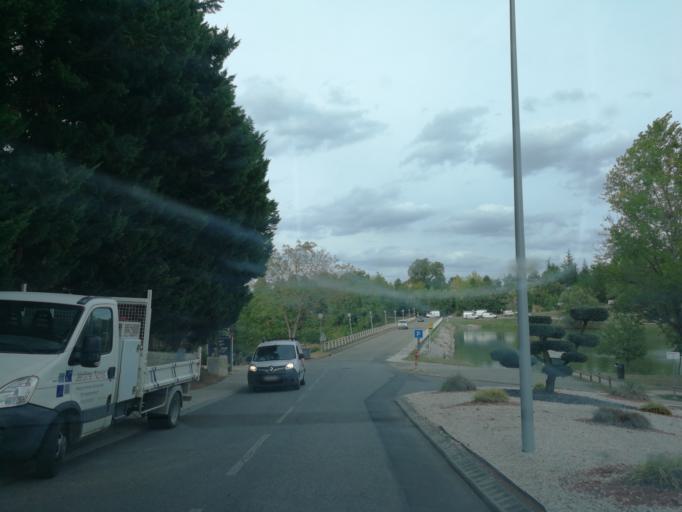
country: FR
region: Midi-Pyrenees
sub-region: Departement de la Haute-Garonne
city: Flourens
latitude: 43.5958
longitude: 1.5638
